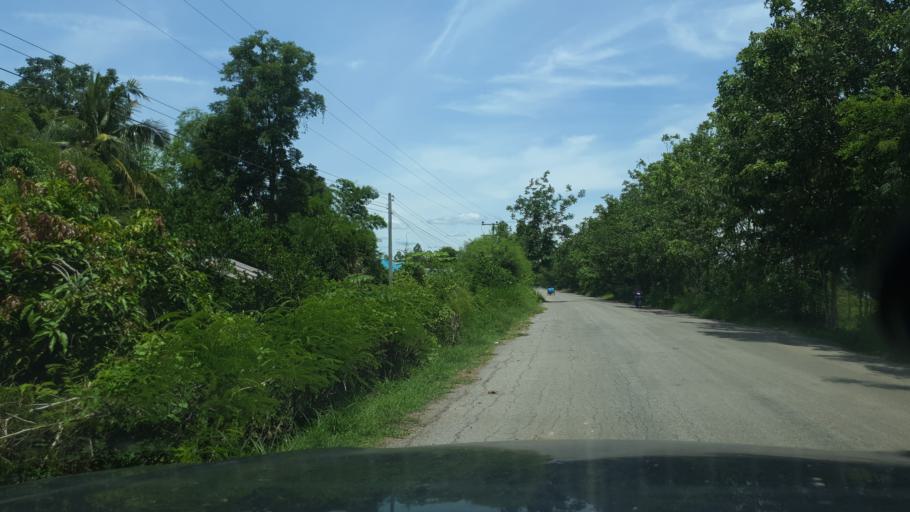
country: TH
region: Sukhothai
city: Ban Na
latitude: 17.0939
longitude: 99.6855
